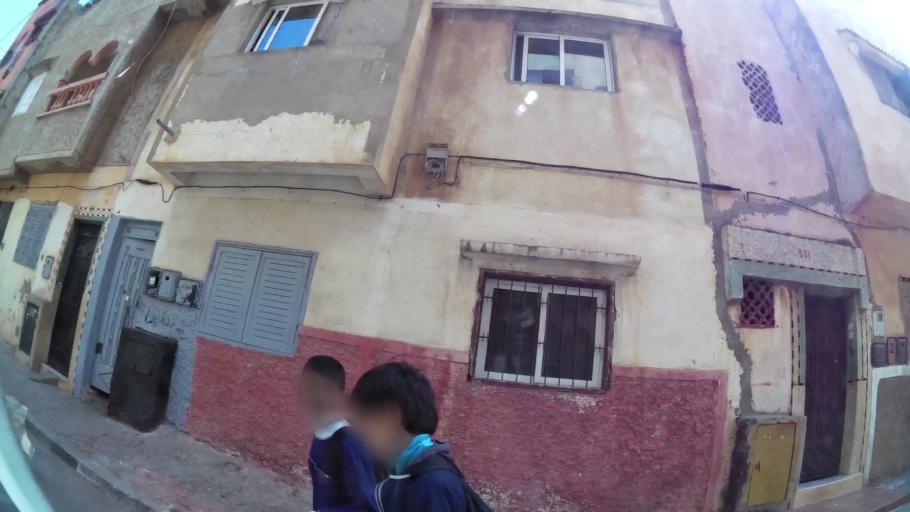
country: MA
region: Rabat-Sale-Zemmour-Zaer
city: Sale
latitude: 34.0660
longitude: -6.7826
